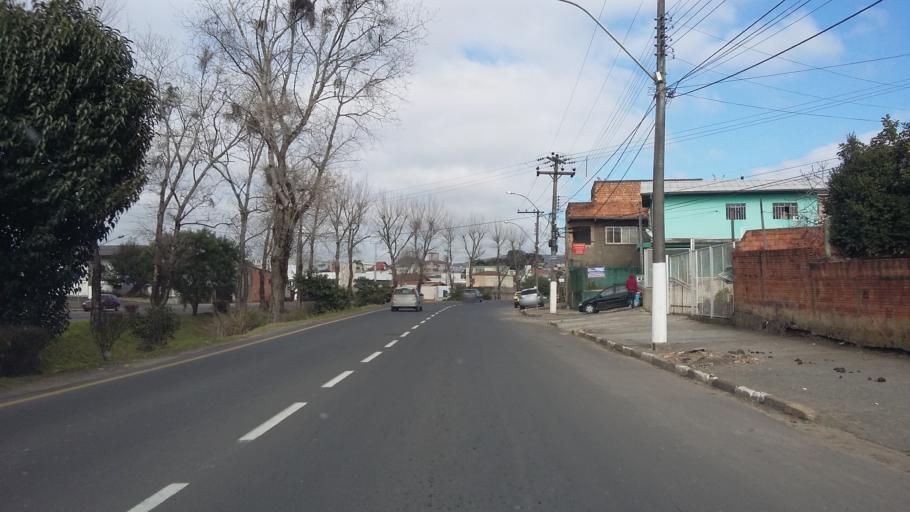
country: BR
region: Santa Catarina
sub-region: Lages
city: Lages
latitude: -27.8118
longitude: -50.3324
